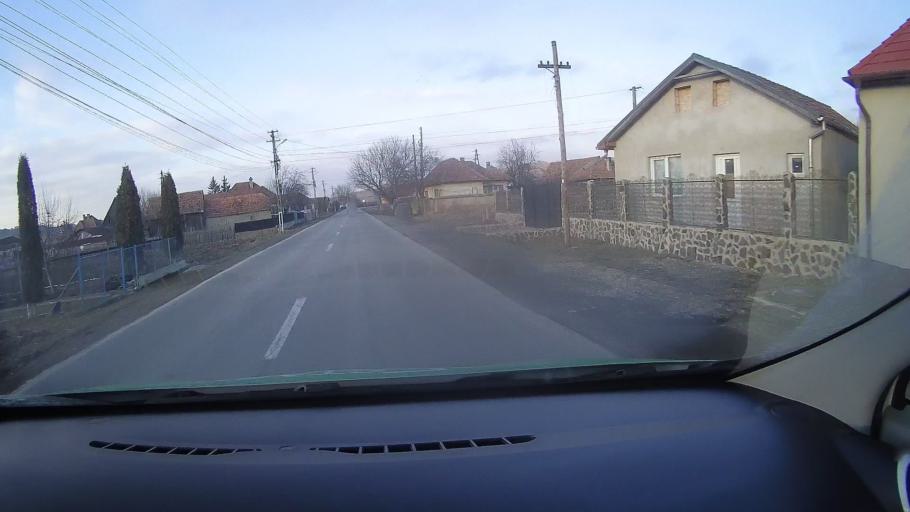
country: RO
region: Mures
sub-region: Comuna Vanatori
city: Vanatori
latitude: 46.2447
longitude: 24.9236
